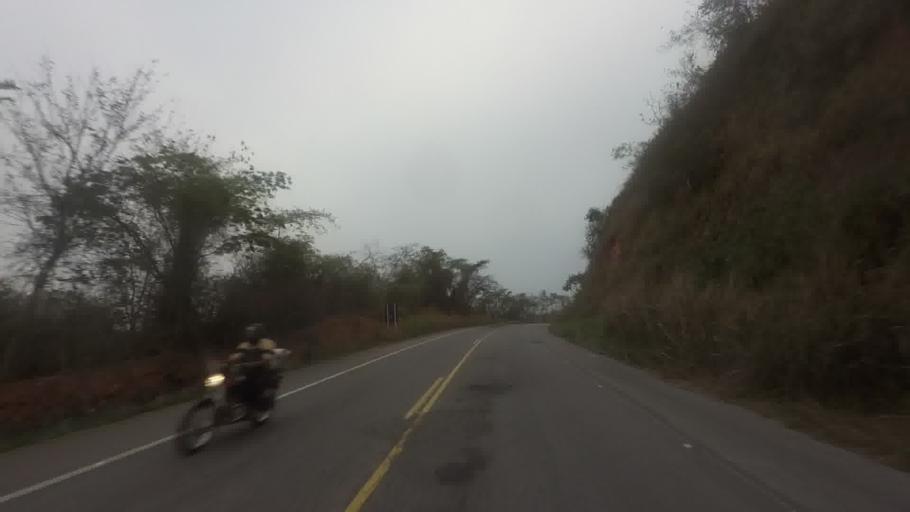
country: BR
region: Rio de Janeiro
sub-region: Santo Antonio De Padua
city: Santo Antonio de Padua
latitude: -21.6573
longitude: -42.3048
